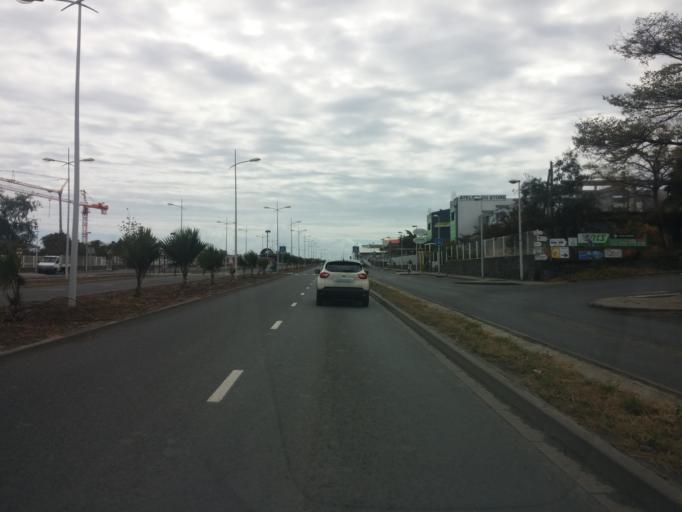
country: RE
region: Reunion
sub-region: Reunion
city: Le Port
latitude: -20.9645
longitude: 55.2946
